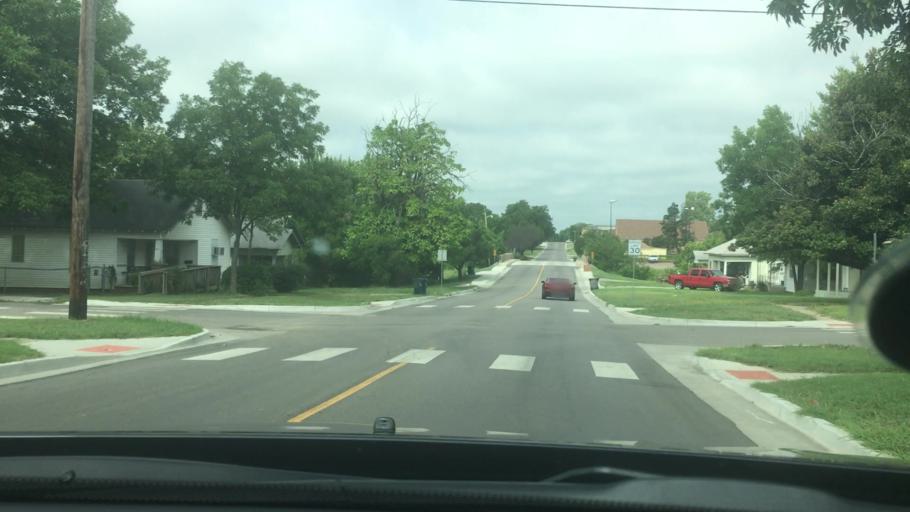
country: US
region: Oklahoma
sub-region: Pontotoc County
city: Ada
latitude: 34.7713
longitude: -96.6719
